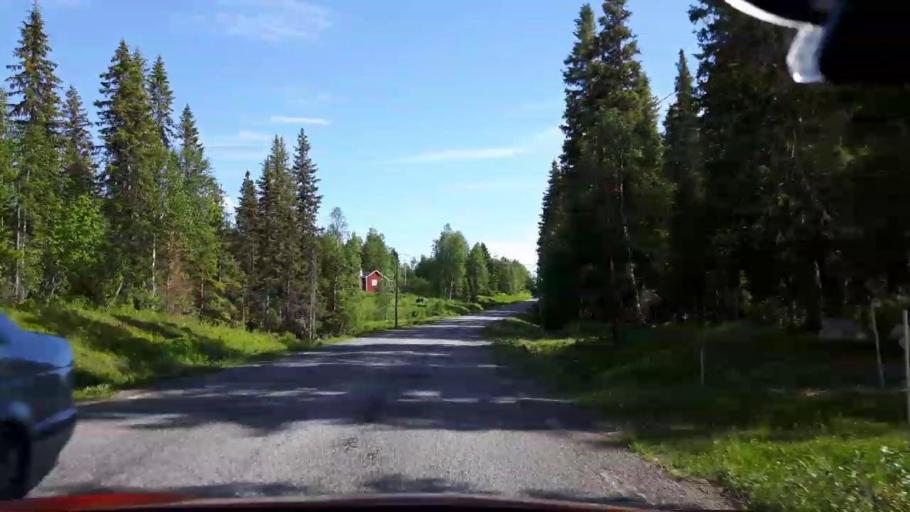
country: SE
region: Jaemtland
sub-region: Krokoms Kommun
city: Valla
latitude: 63.7509
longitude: 14.1165
